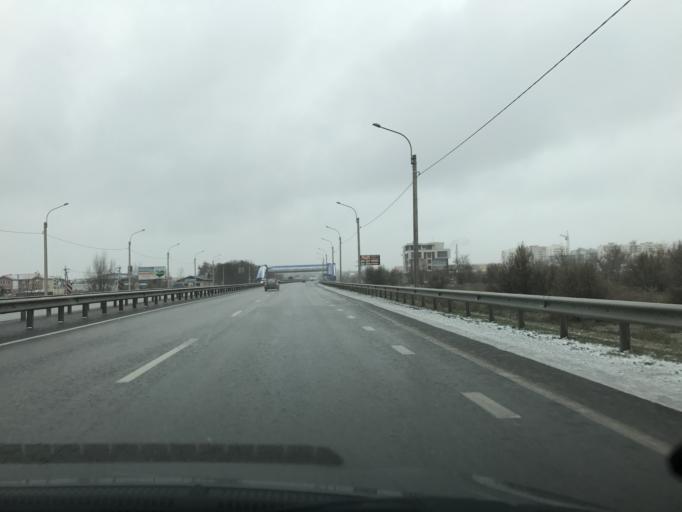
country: RU
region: Rostov
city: Bataysk
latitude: 47.1419
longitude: 39.7758
